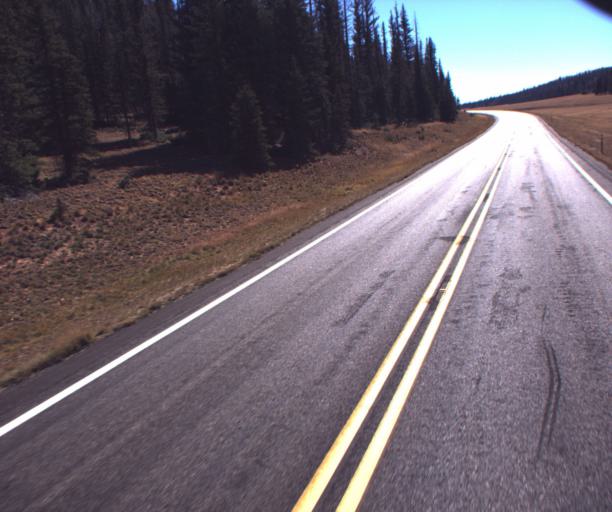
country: US
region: Arizona
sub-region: Coconino County
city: Grand Canyon
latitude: 36.3795
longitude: -112.1260
